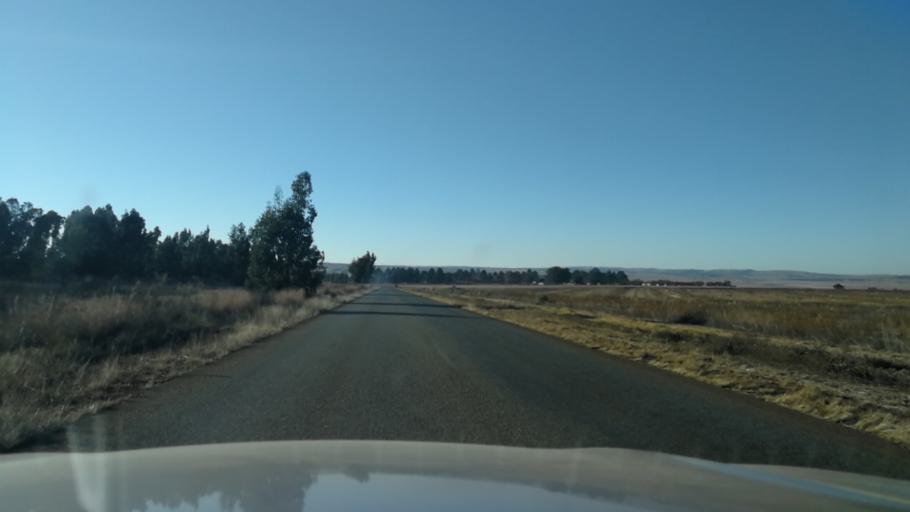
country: ZA
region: North-West
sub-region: Bojanala Platinum District Municipality
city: Rustenburg
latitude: -25.9679
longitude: 27.2232
